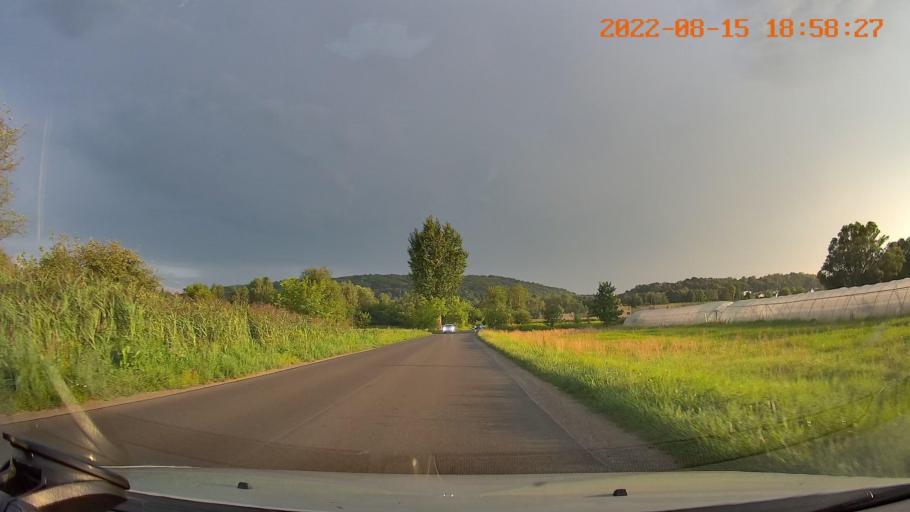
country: PL
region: Lesser Poland Voivodeship
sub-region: Powiat krakowski
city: Rzaska
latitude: 50.0753
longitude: 19.8493
